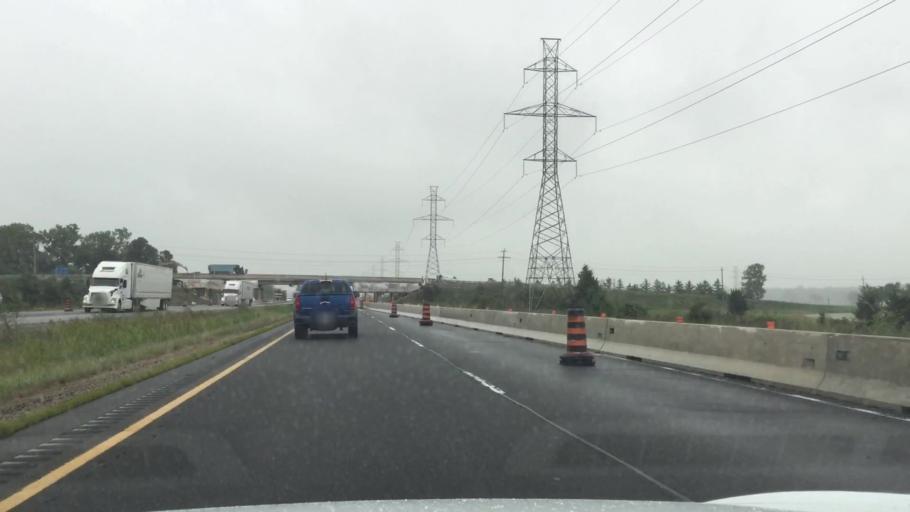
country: CA
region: Ontario
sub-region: Lambton County
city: Walpole Island
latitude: 42.3675
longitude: -82.1428
